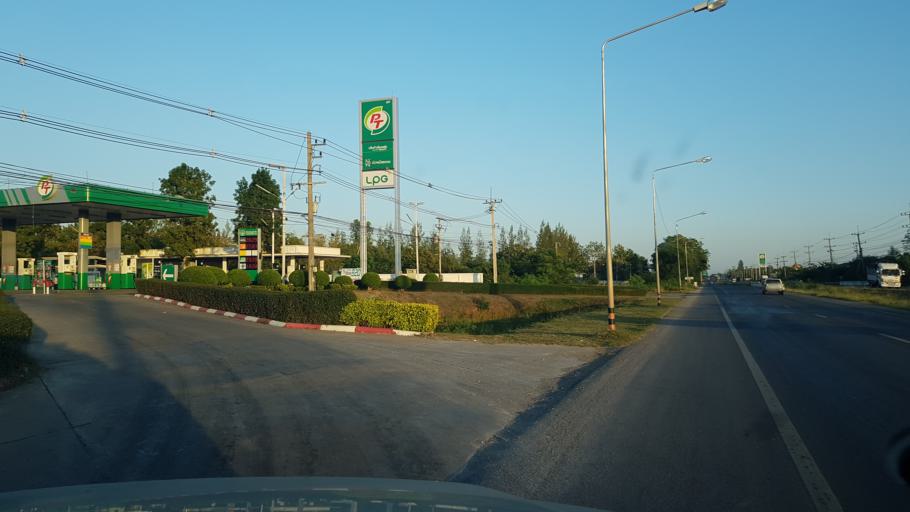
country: TH
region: Khon Kaen
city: Chum Phae
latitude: 16.5806
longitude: 102.0190
